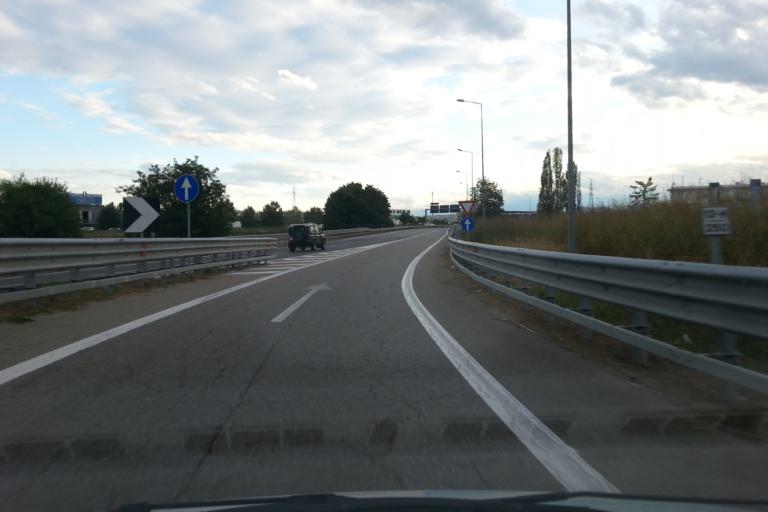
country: IT
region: Piedmont
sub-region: Provincia di Torino
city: Savonera
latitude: 45.1055
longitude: 7.5976
